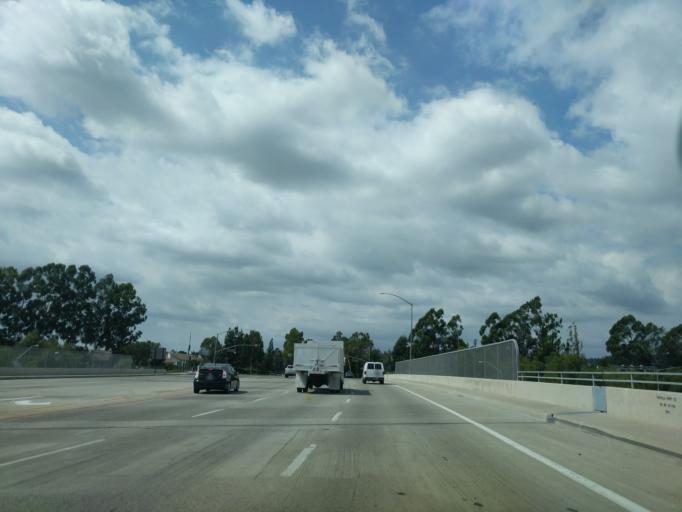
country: US
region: California
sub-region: Orange County
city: North Tustin
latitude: 33.7407
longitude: -117.7666
